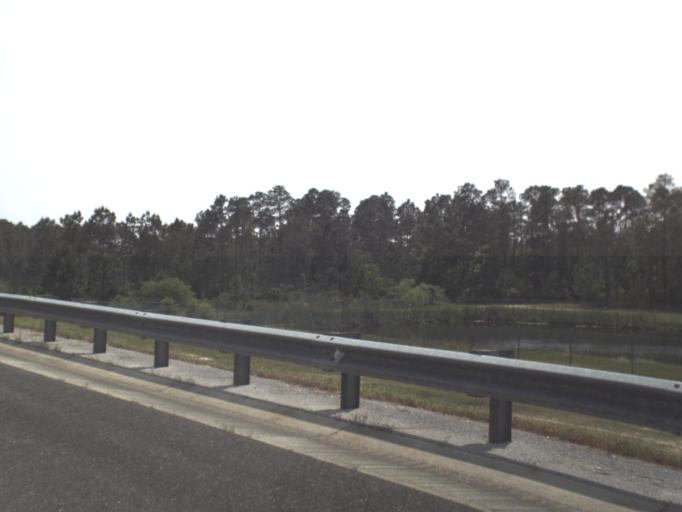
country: US
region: Florida
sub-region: Santa Rosa County
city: Bagdad
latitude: 30.5255
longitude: -87.0873
